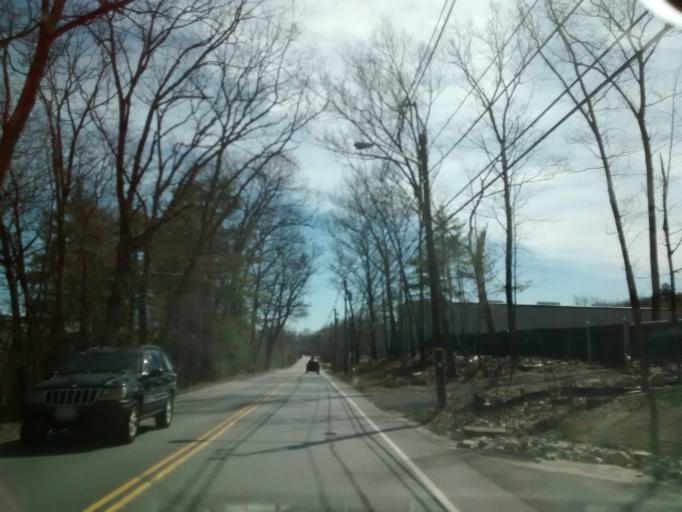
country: US
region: Massachusetts
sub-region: Worcester County
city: Whitinsville
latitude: 42.1083
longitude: -71.6750
